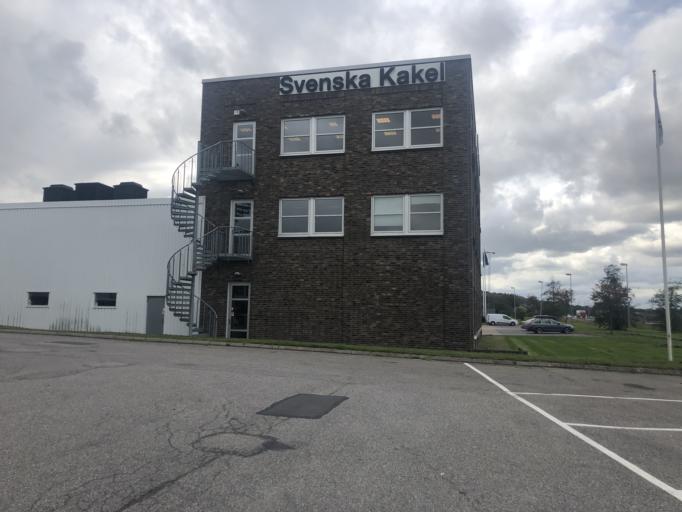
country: SE
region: Vaestra Goetaland
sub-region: Molndal
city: Moelndal
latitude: 57.6440
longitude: 12.0116
